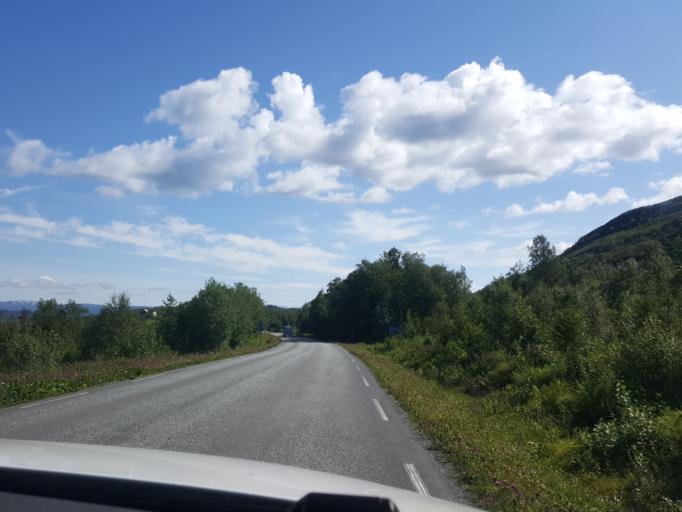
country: NO
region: Nordland
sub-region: Bodo
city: Loding
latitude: 67.2284
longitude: 14.8896
